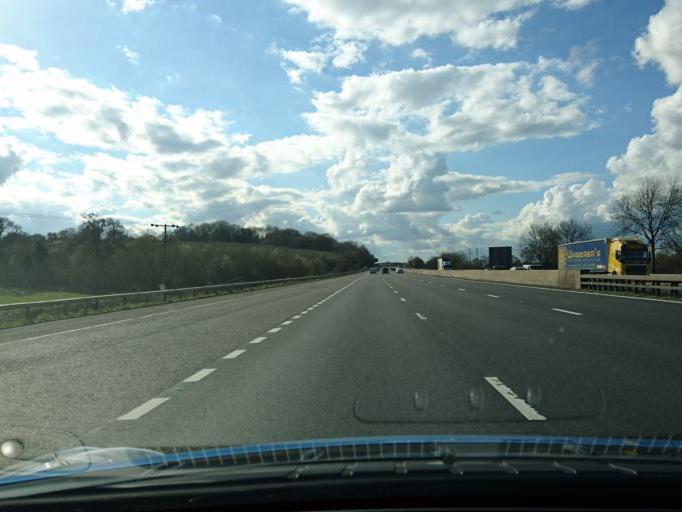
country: GB
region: England
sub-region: Borough of Swindon
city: Chiseldon
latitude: 51.5276
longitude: -1.7315
